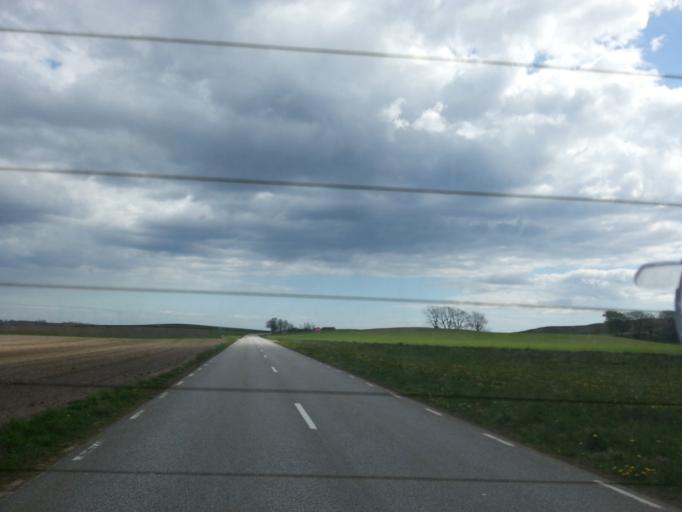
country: SE
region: Skane
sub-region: Ystads Kommun
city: Kopingebro
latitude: 55.4052
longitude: 14.0220
